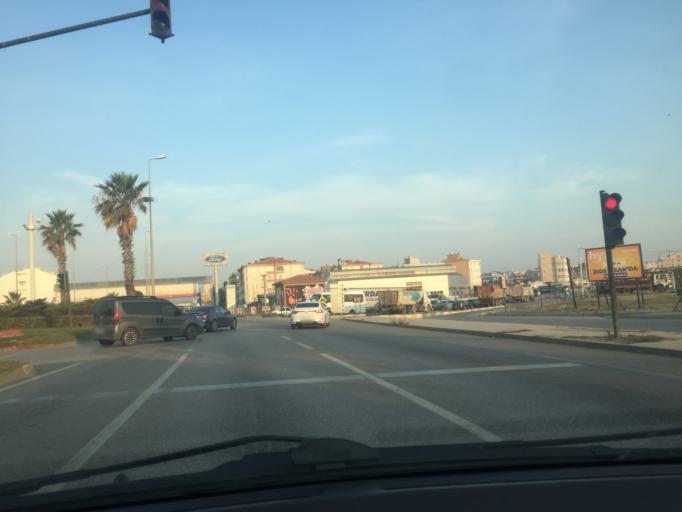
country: TR
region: Balikesir
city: Bandirma
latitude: 40.3339
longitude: 27.9931
